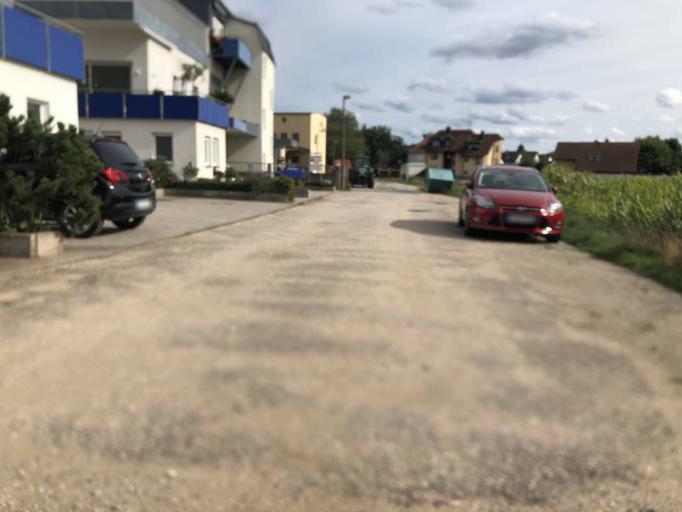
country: DE
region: Bavaria
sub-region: Regierungsbezirk Mittelfranken
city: Furth
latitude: 49.5176
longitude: 10.9821
